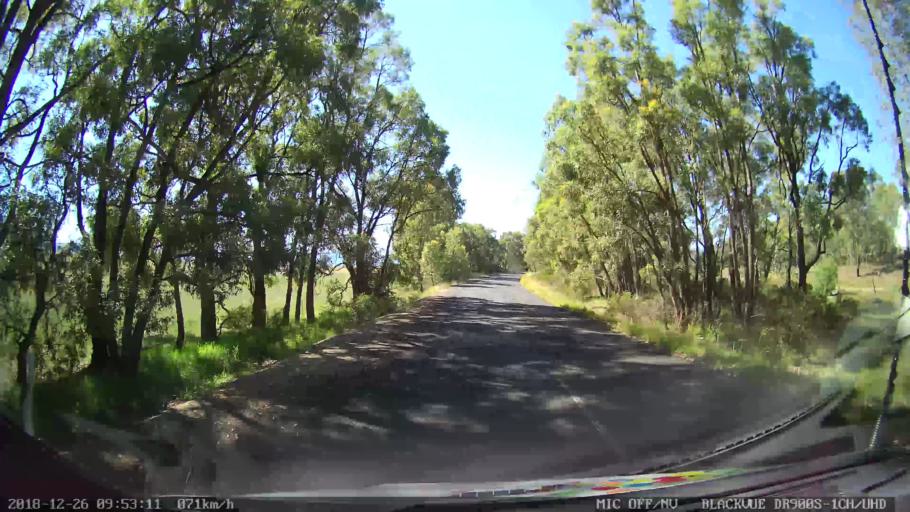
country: AU
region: New South Wales
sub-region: Mid-Western Regional
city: Kandos
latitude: -33.0182
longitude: 150.1525
